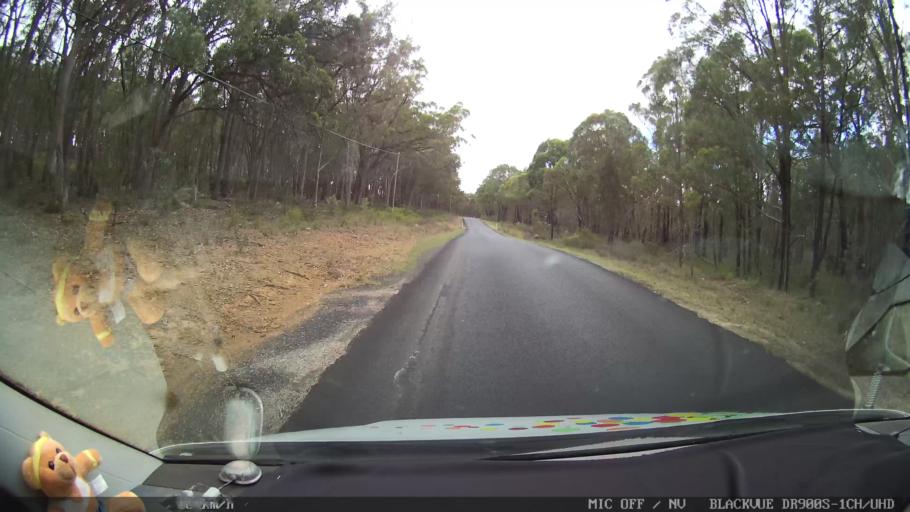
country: AU
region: New South Wales
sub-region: Glen Innes Severn
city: Glen Innes
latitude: -29.4349
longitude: 151.6318
